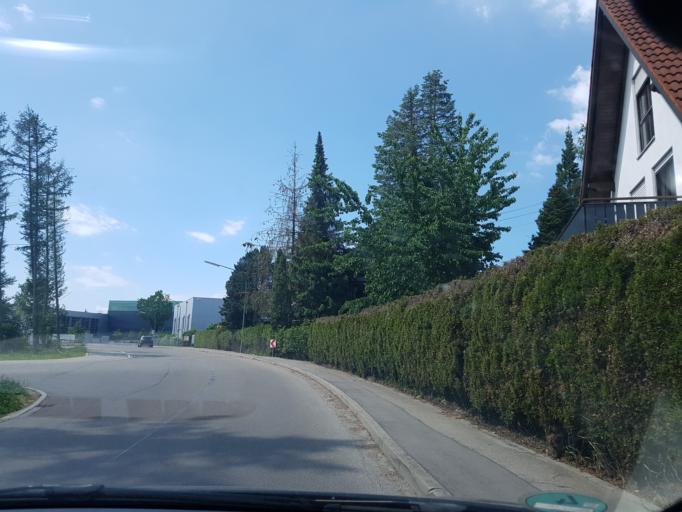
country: DE
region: Bavaria
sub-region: Swabia
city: Nersingen
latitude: 48.4182
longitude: 10.1555
